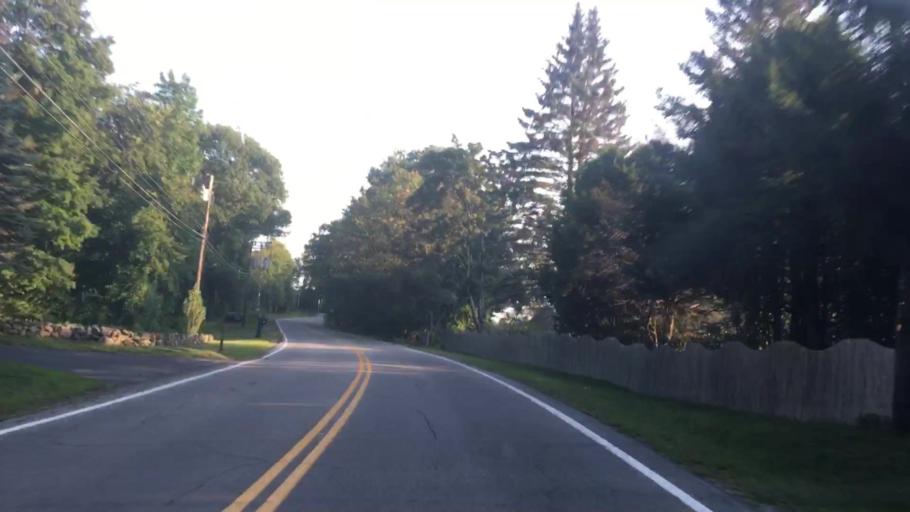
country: US
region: New Hampshire
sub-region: Belknap County
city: Gilmanton
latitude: 43.4756
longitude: -71.4295
